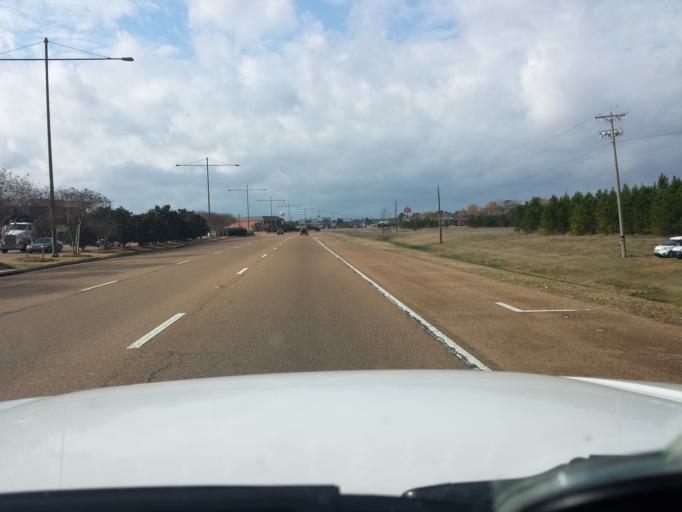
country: US
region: Mississippi
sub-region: Rankin County
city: Flowood
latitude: 32.3352
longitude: -90.0985
